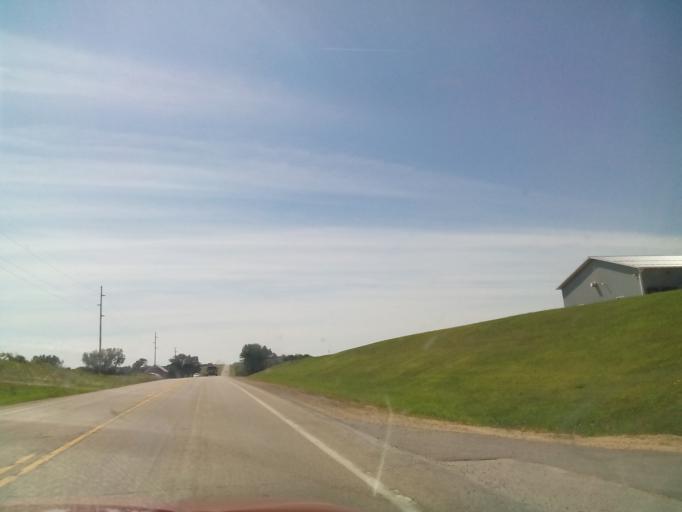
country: US
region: Wisconsin
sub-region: Green County
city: Monticello
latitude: 42.7030
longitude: -89.6171
